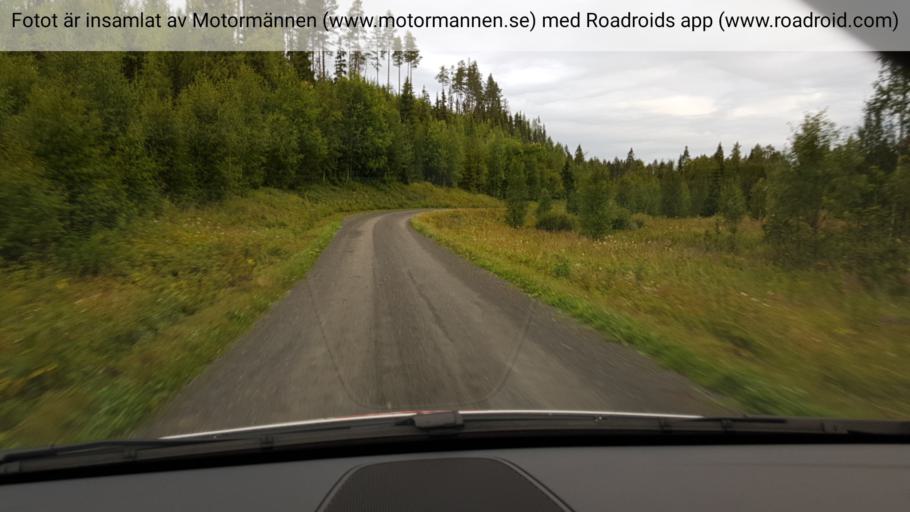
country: SE
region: Jaemtland
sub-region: OEstersunds Kommun
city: Lit
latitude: 63.5025
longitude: 14.7424
